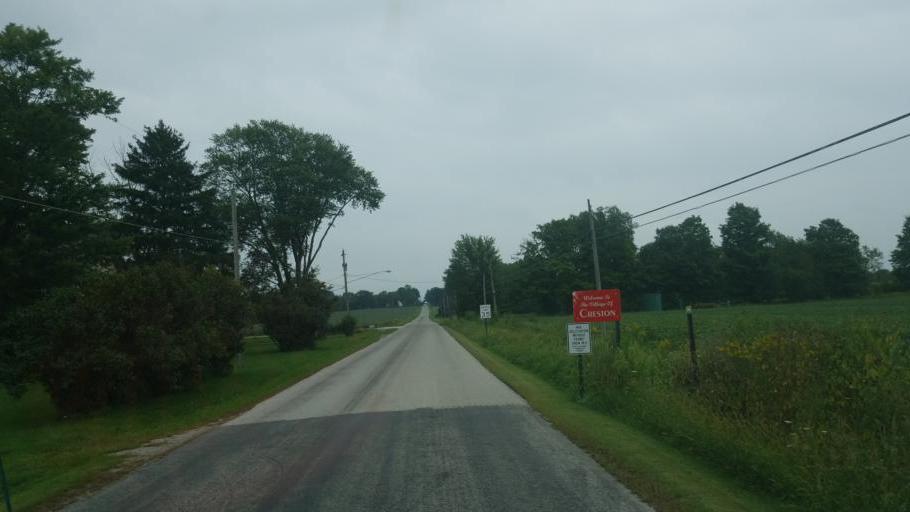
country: US
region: Ohio
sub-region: Wayne County
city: Creston
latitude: 40.9600
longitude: -81.9103
